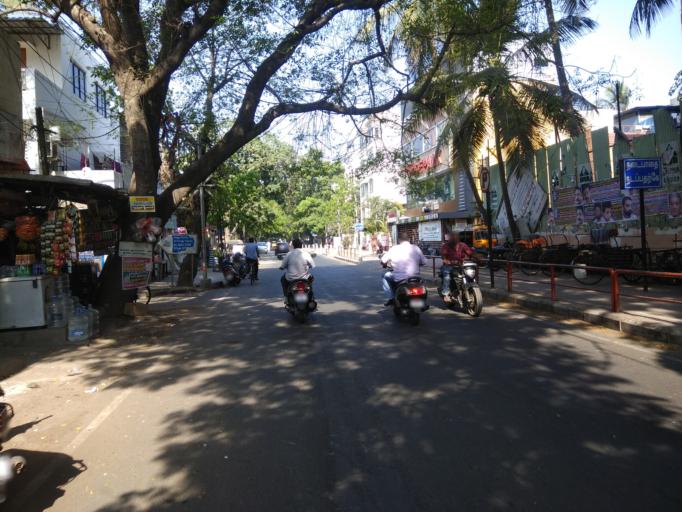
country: IN
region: Tamil Nadu
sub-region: Kancheepuram
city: Saint Thomas Mount
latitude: 13.0414
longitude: 80.1969
